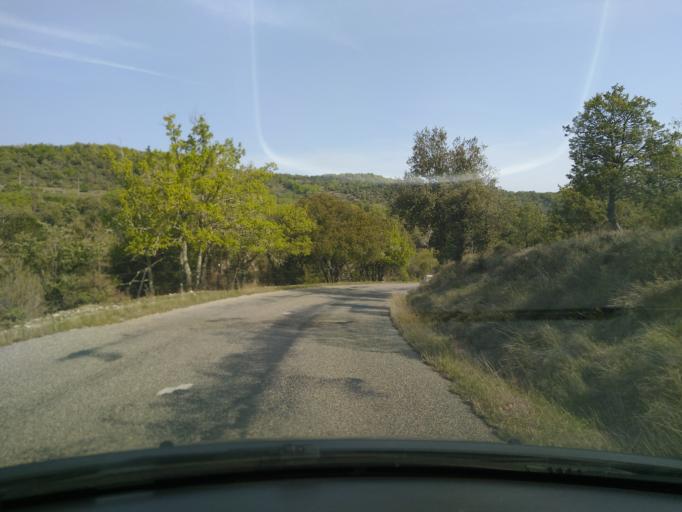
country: FR
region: Rhone-Alpes
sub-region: Departement de l'Ardeche
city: Ruoms
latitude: 44.4512
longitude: 4.3874
